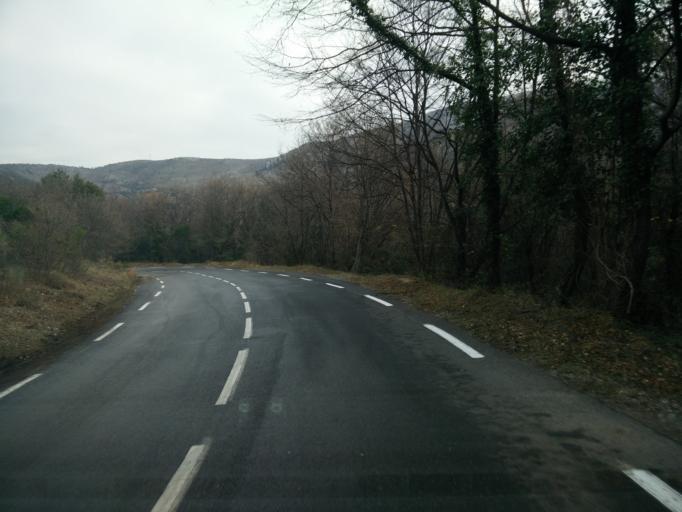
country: FR
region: Provence-Alpes-Cote d'Azur
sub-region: Departement des Alpes-Maritimes
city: Tourrettes-sur-Loup
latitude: 43.7391
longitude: 6.9954
